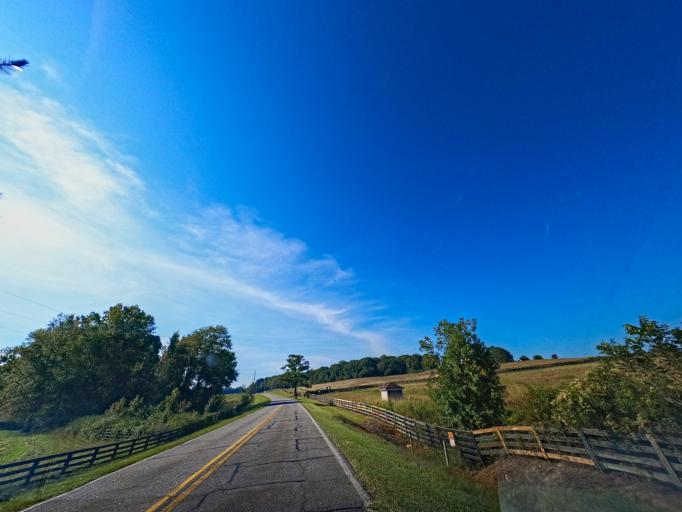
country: US
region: Georgia
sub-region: Coweta County
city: Grantville
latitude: 33.3044
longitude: -84.9284
